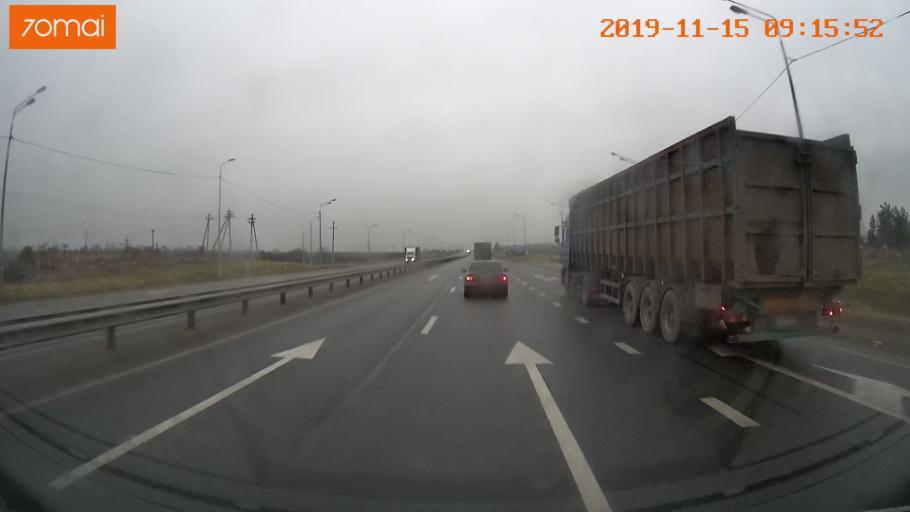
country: RU
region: Vologda
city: Tonshalovo
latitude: 59.2439
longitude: 37.9696
